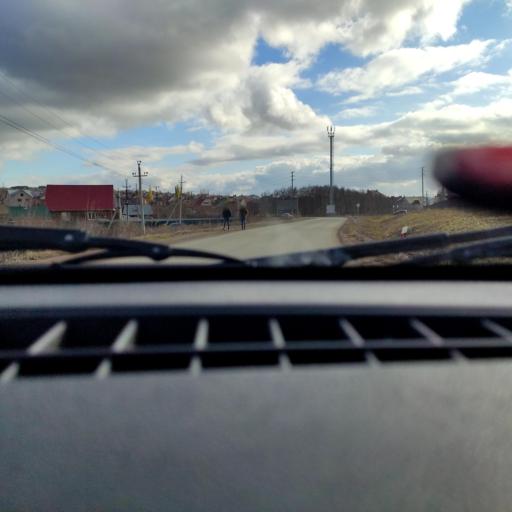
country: RU
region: Bashkortostan
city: Ufa
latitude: 54.5996
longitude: 55.9247
